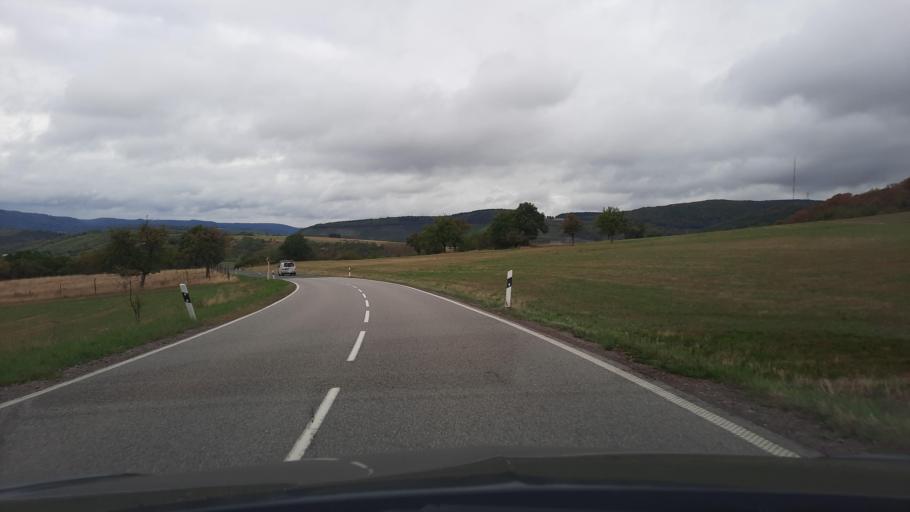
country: DE
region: Rheinland-Pfalz
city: Irsch
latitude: 49.5978
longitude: 6.5948
